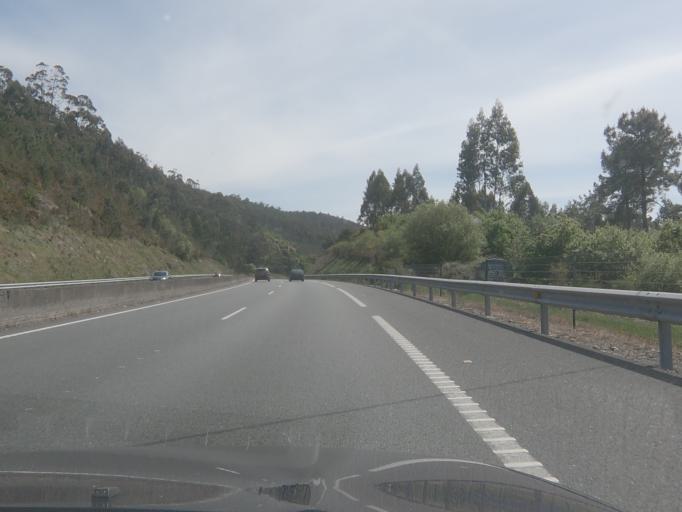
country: ES
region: Galicia
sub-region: Provincia da Coruna
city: Padron
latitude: 42.7689
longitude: -8.6447
